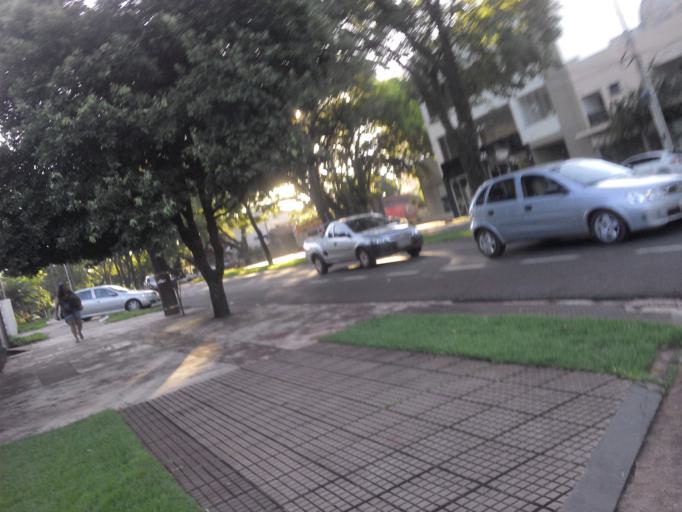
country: BR
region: Parana
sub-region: Maringa
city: Maringa
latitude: -23.4370
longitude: -51.9361
